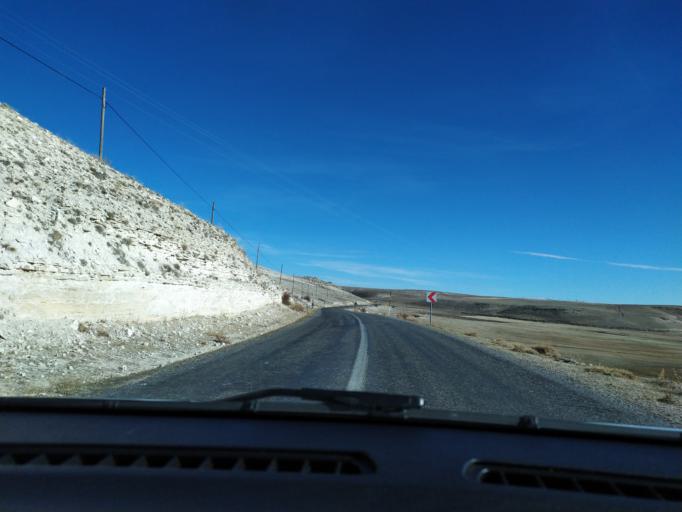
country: TR
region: Kayseri
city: Orensehir
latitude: 38.9786
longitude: 36.6646
